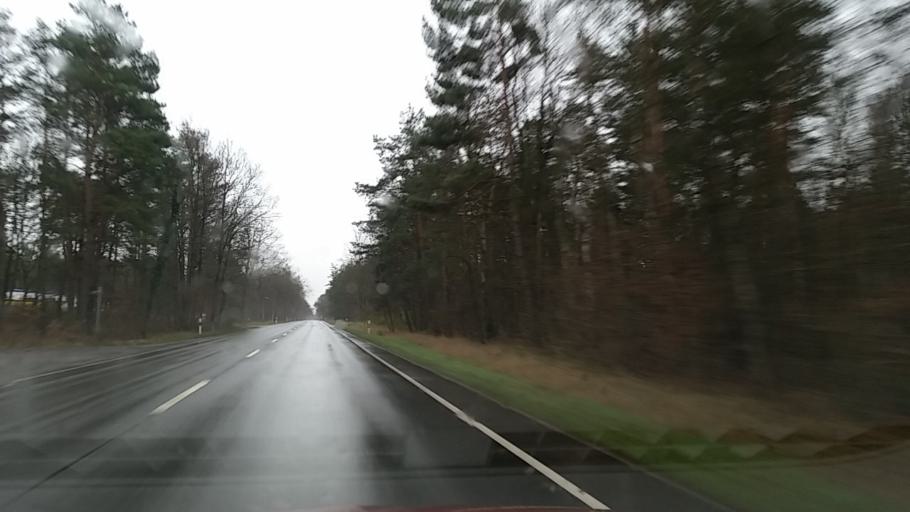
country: DE
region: Lower Saxony
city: Wagenhoff
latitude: 52.5627
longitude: 10.5078
